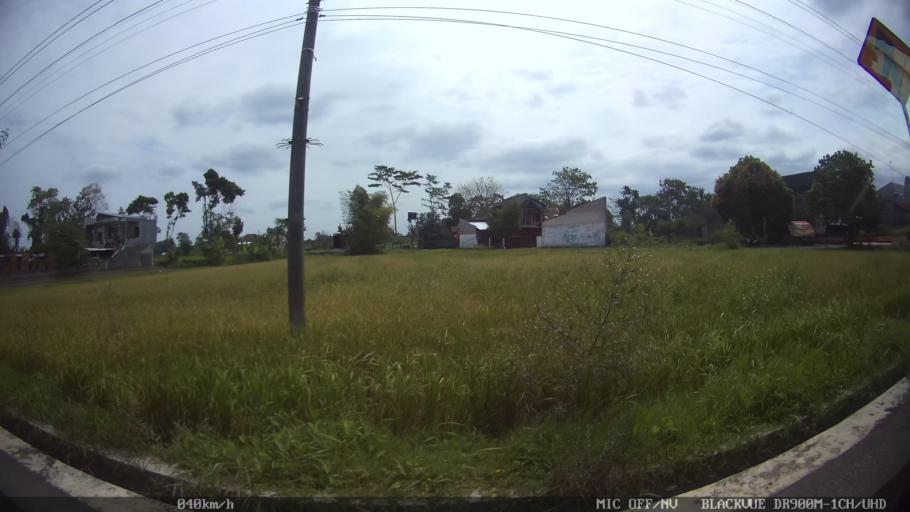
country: ID
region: Central Java
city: Candi Prambanan
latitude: -7.7419
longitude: 110.4814
